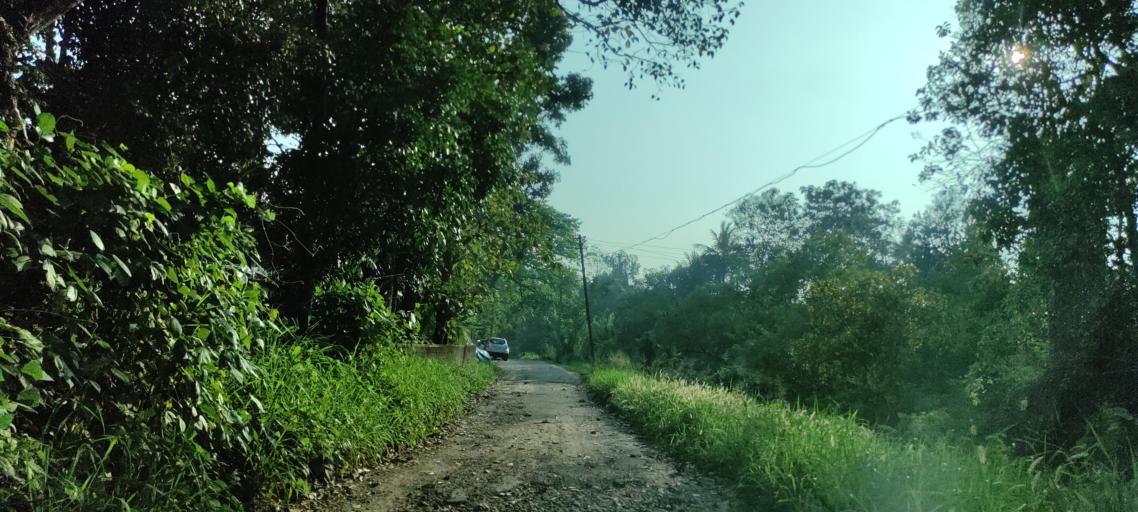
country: IN
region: Kerala
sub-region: Pattanamtitta
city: Adur
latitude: 9.1418
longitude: 76.7331
